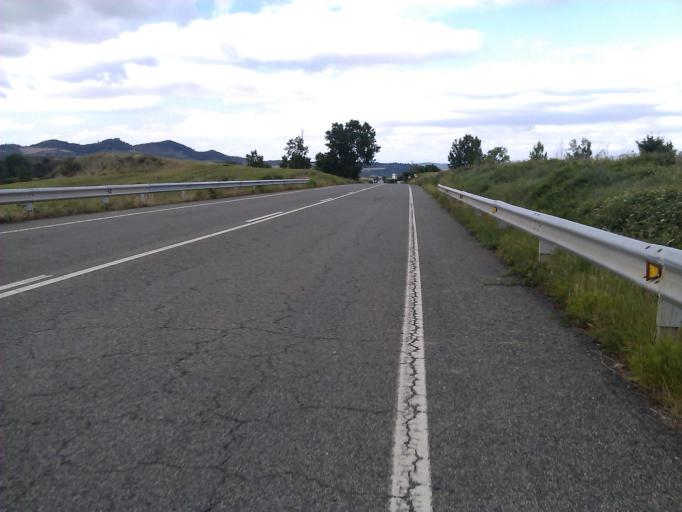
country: ES
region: Navarre
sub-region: Provincia de Navarra
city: Obanos
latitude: 42.6978
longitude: -1.7871
